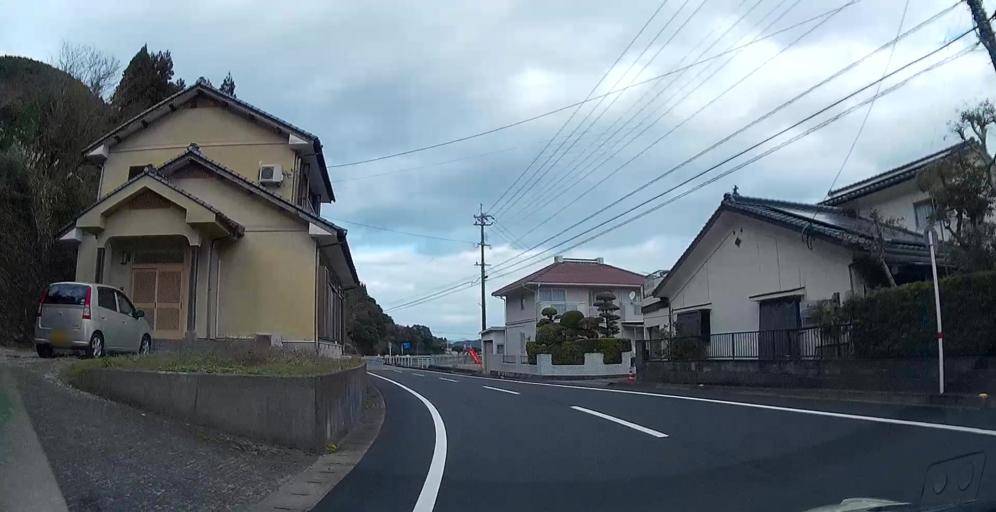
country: JP
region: Kumamoto
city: Minamata
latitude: 32.1977
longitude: 130.4072
